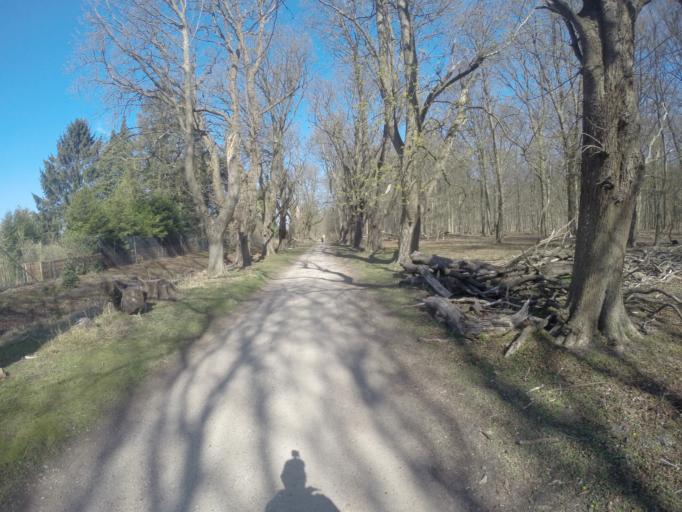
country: DK
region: Capital Region
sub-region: Lyngby-Tarbaek Kommune
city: Kongens Lyngby
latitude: 55.7903
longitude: 12.5447
